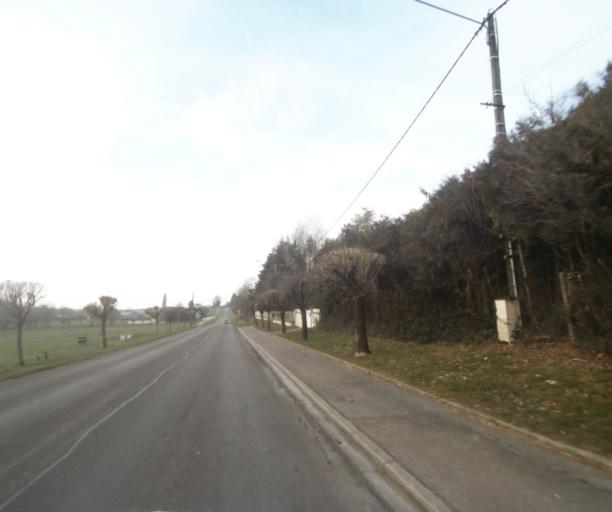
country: FR
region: Champagne-Ardenne
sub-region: Departement de la Haute-Marne
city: Chancenay
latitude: 48.6662
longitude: 4.9814
